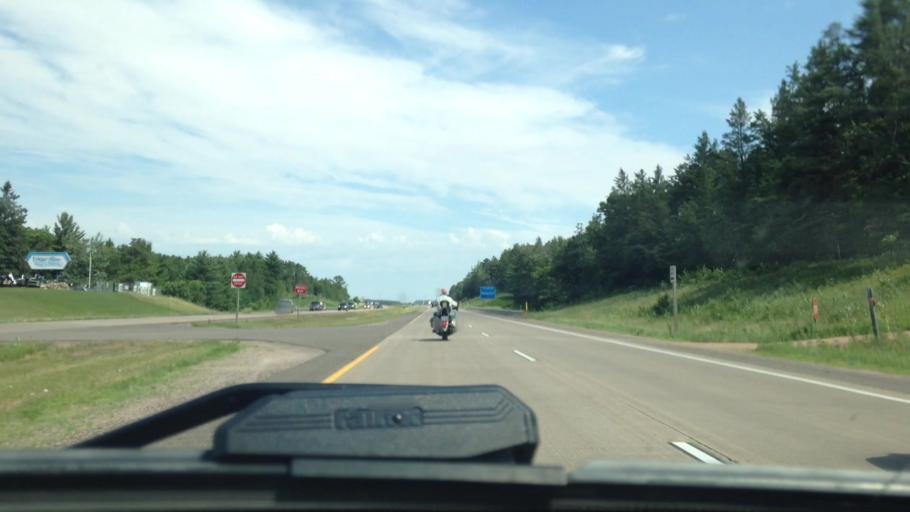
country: US
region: Wisconsin
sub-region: Washburn County
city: Spooner
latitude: 45.8902
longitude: -91.8276
